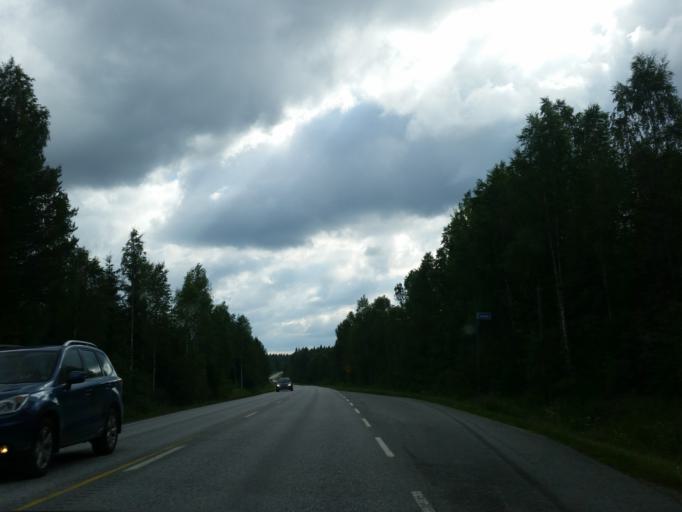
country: FI
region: Northern Savo
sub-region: Kuopio
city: Karttula
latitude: 62.8576
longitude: 27.2176
